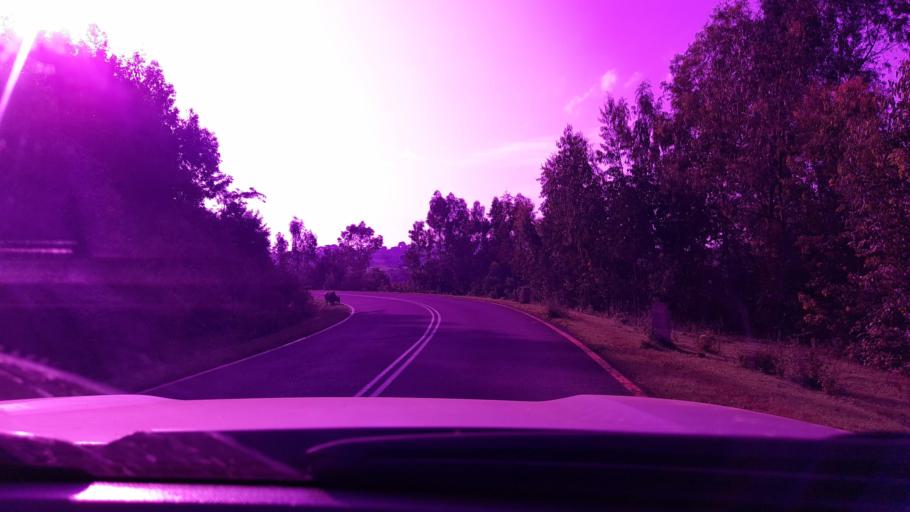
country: ET
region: Oromiya
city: Bedele
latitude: 8.1394
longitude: 36.4549
